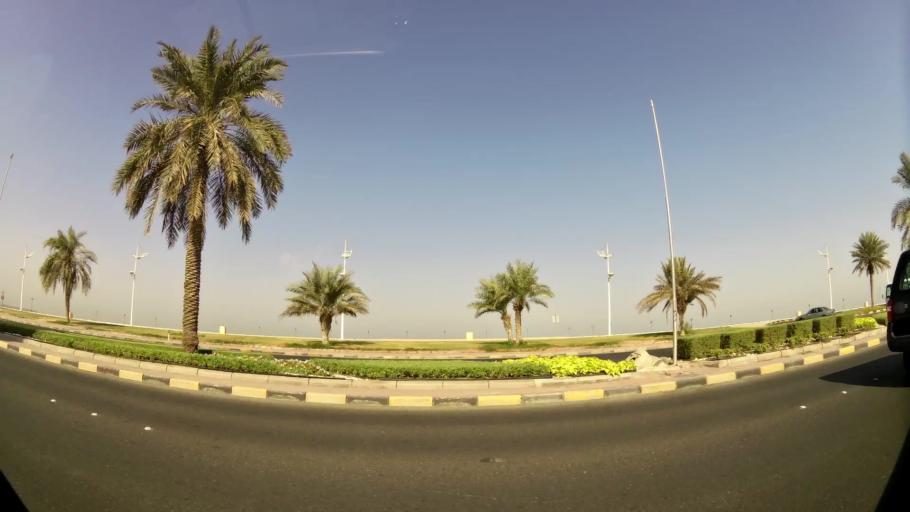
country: KW
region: Al Asimah
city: Kuwait City
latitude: 29.3731
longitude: 47.9649
